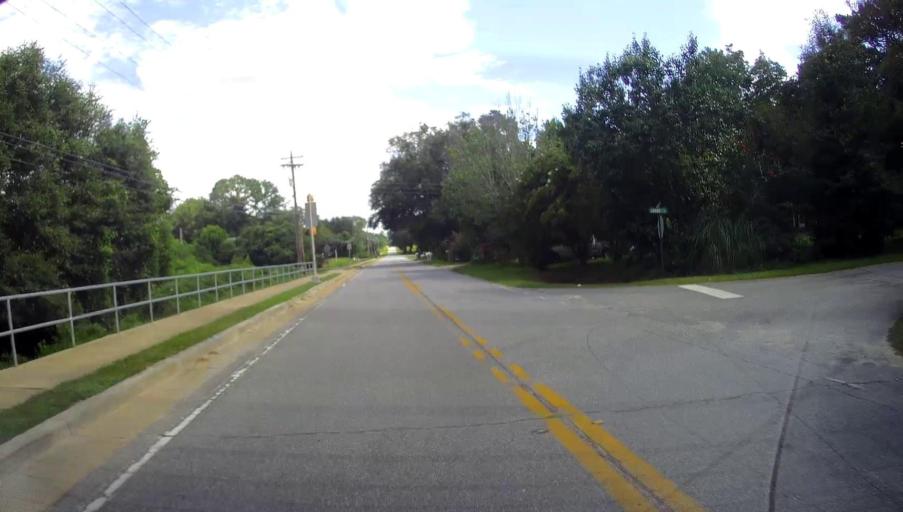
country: US
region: Georgia
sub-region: Chattahoochee County
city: Cusseta
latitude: 32.3006
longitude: -84.7709
